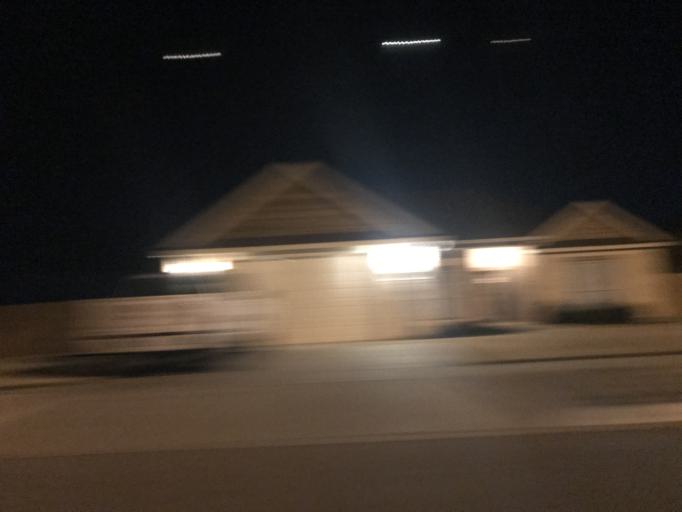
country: US
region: Texas
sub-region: Taylor County
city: Potosi
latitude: 32.3726
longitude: -99.7181
